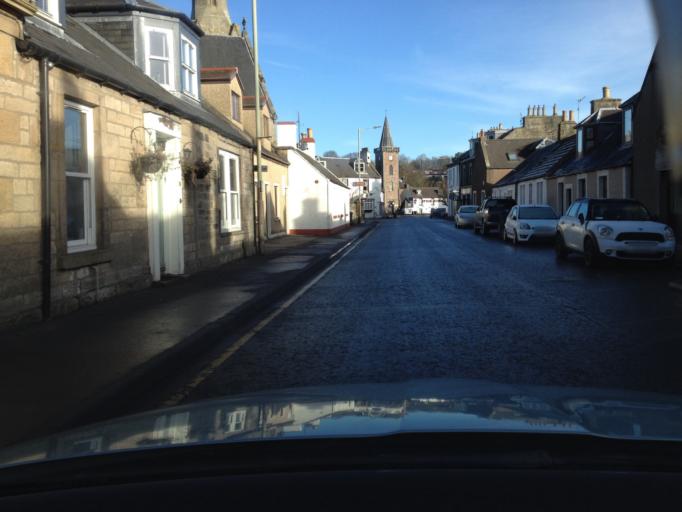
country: GB
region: Scotland
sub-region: Perth and Kinross
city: Milnathort
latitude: 56.2256
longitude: -3.4211
